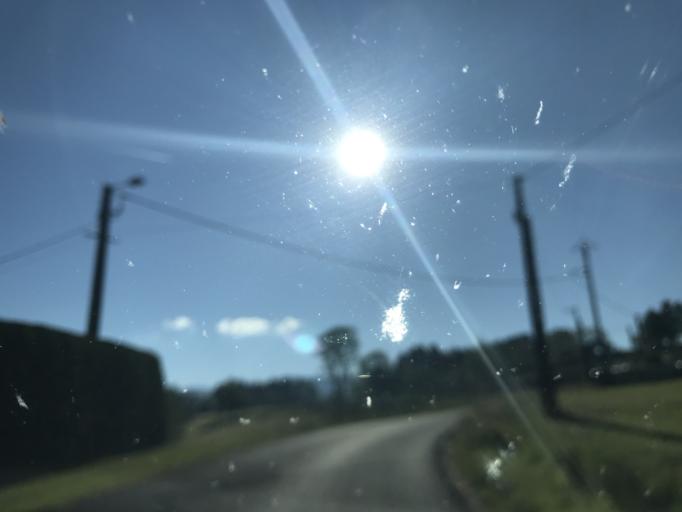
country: FR
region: Auvergne
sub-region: Departement du Puy-de-Dome
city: Job
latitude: 45.6384
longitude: 3.6723
